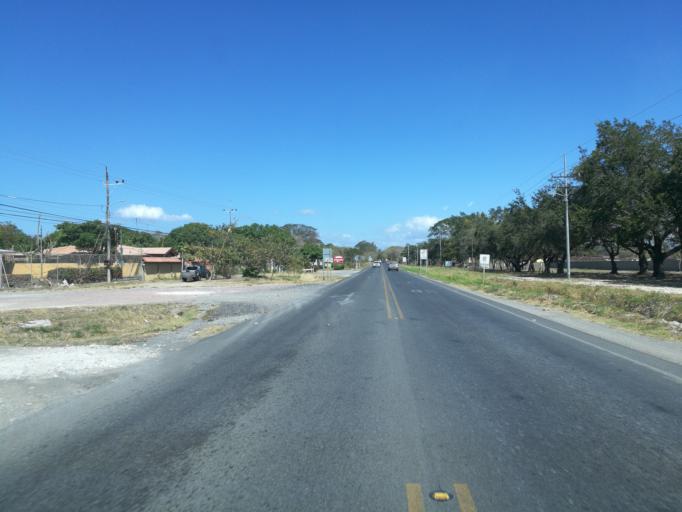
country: CR
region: Guanacaste
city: Liberia
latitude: 10.6388
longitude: -85.4516
